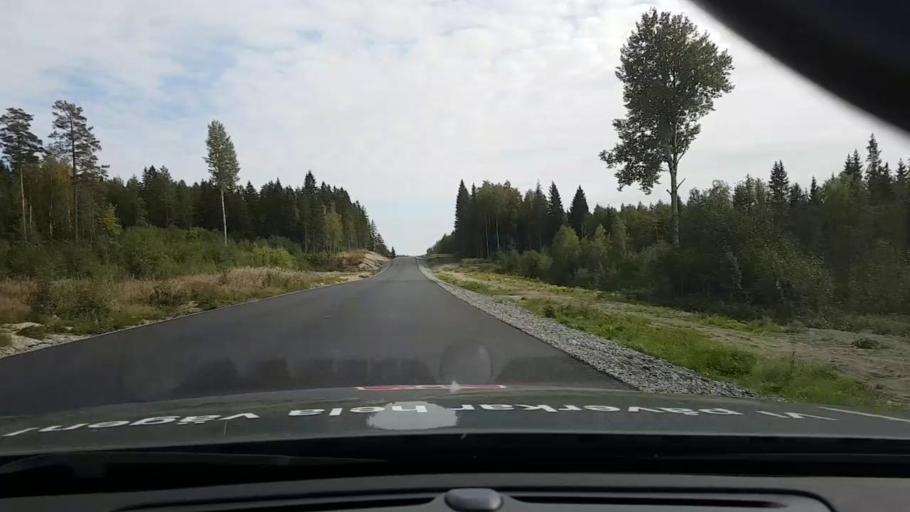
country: SE
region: Vaesternorrland
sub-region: OErnskoeldsviks Kommun
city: Bjasta
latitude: 63.2925
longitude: 18.5001
